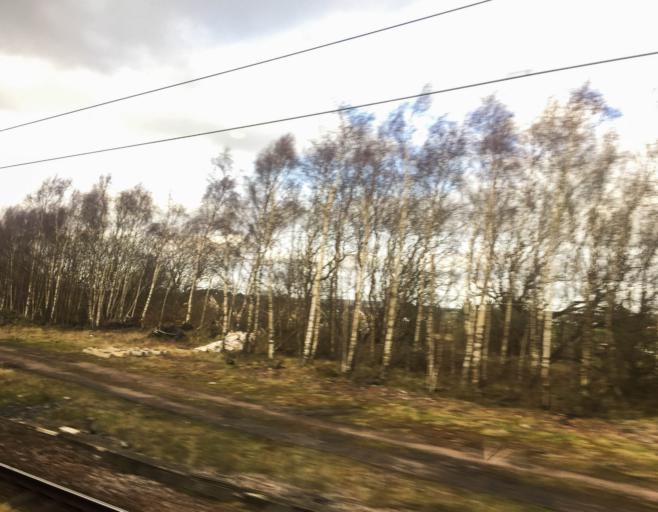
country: GB
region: Scotland
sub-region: South Lanarkshire
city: Law
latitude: 55.7536
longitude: -3.8702
